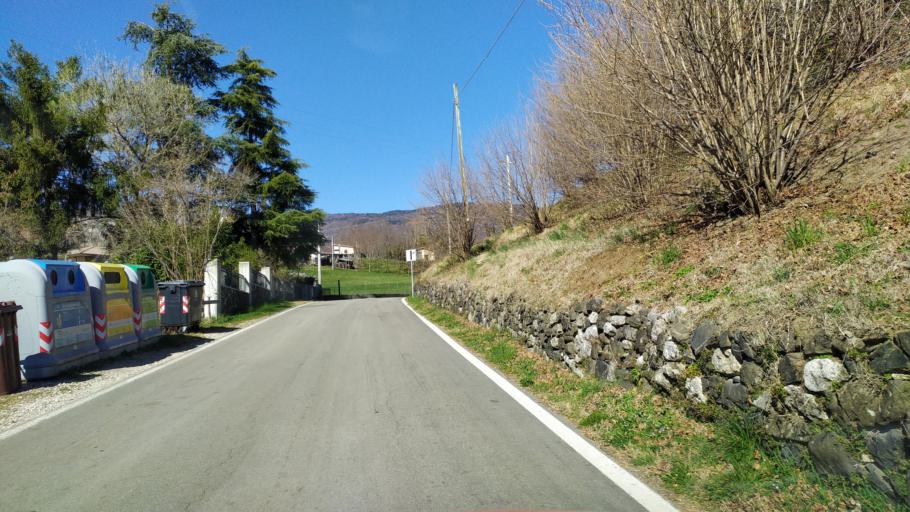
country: IT
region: Veneto
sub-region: Provincia di Vicenza
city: Fara Vicentino
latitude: 45.7498
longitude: 11.5433
